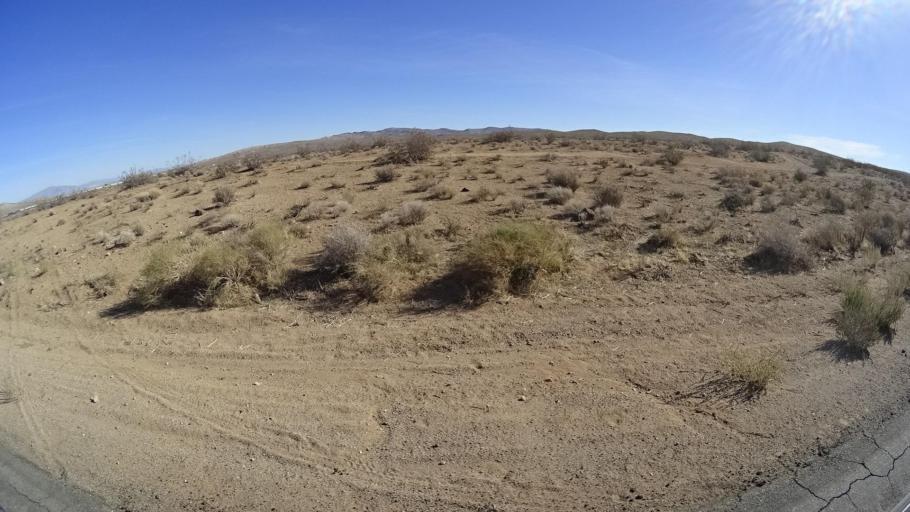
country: US
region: California
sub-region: Kern County
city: Ridgecrest
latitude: 35.4808
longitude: -117.6450
